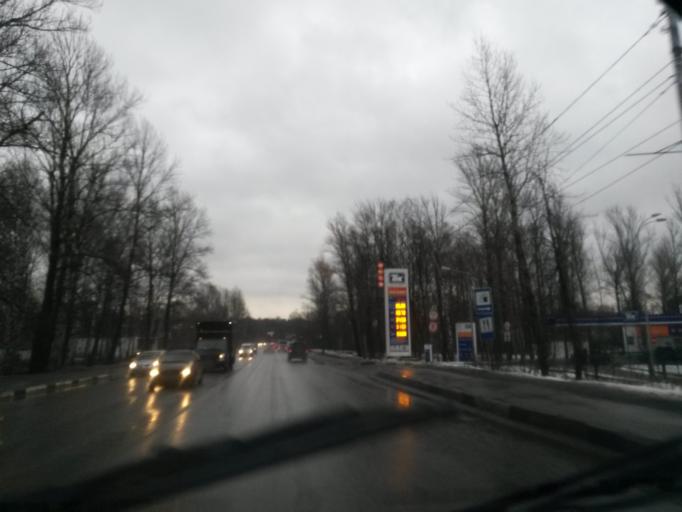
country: RU
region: Jaroslavl
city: Yaroslavl
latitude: 57.6442
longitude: 39.9122
